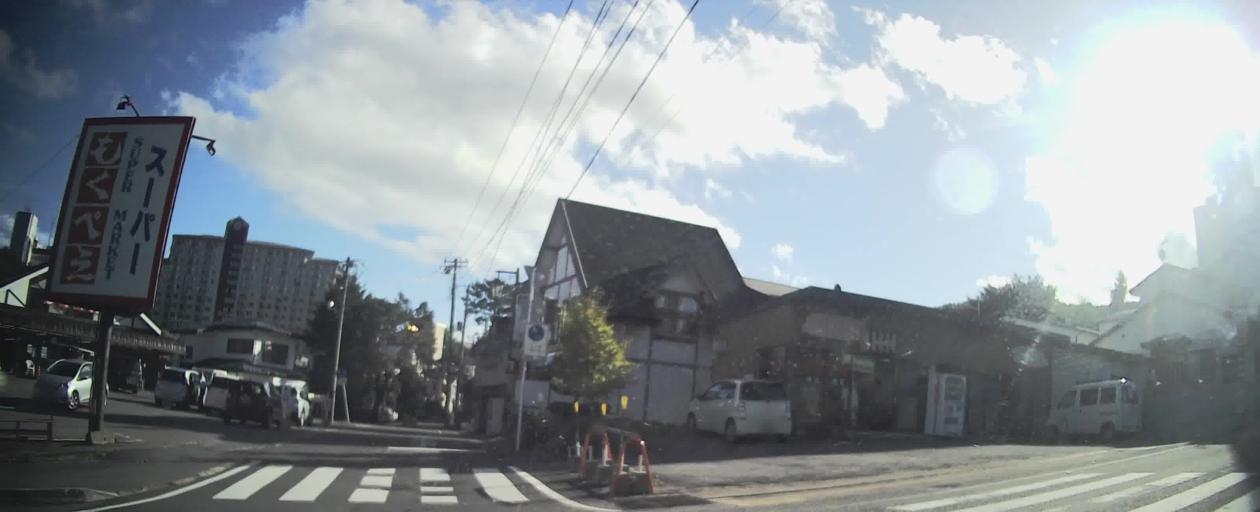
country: JP
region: Gunma
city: Nakanojomachi
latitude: 36.6208
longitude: 138.5944
